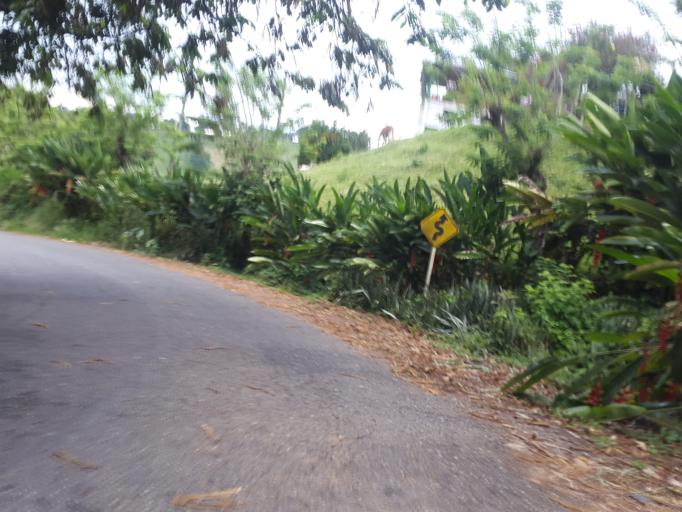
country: CO
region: Quindio
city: Buenavista
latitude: 4.3677
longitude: -75.7586
